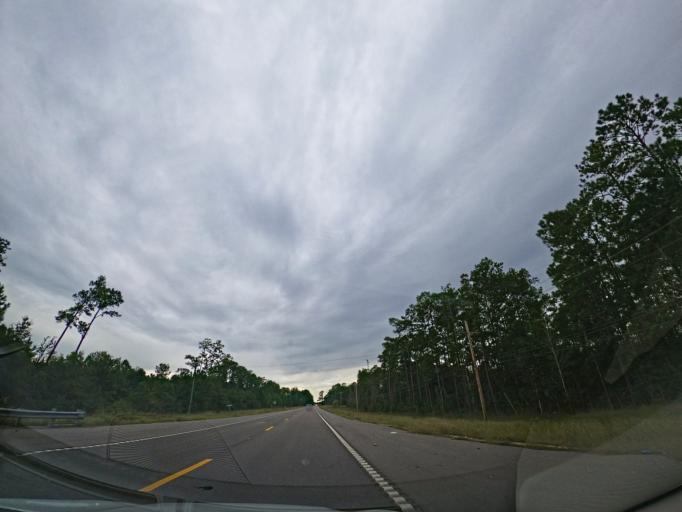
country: US
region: Mississippi
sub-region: Hancock County
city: Pearlington
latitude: 30.2505
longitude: -89.5906
